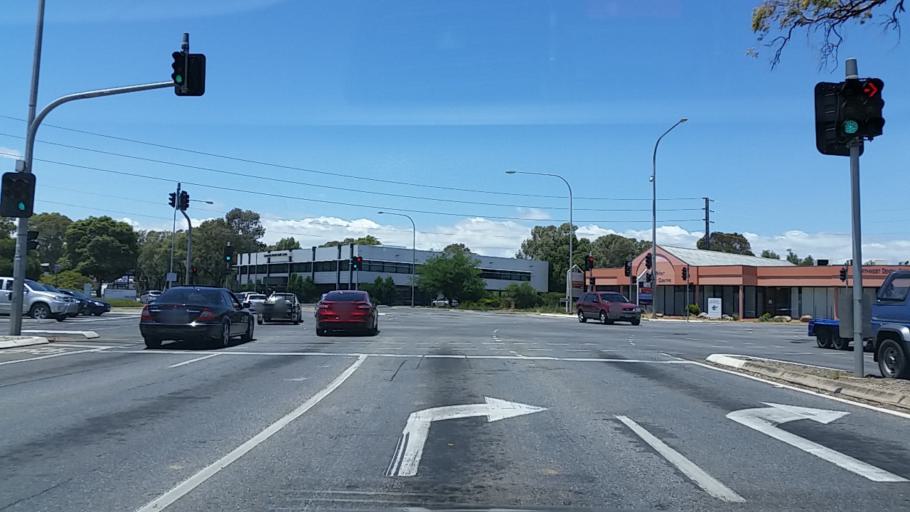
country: AU
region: South Australia
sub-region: Salisbury
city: Salisbury
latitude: -34.7634
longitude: 138.6401
